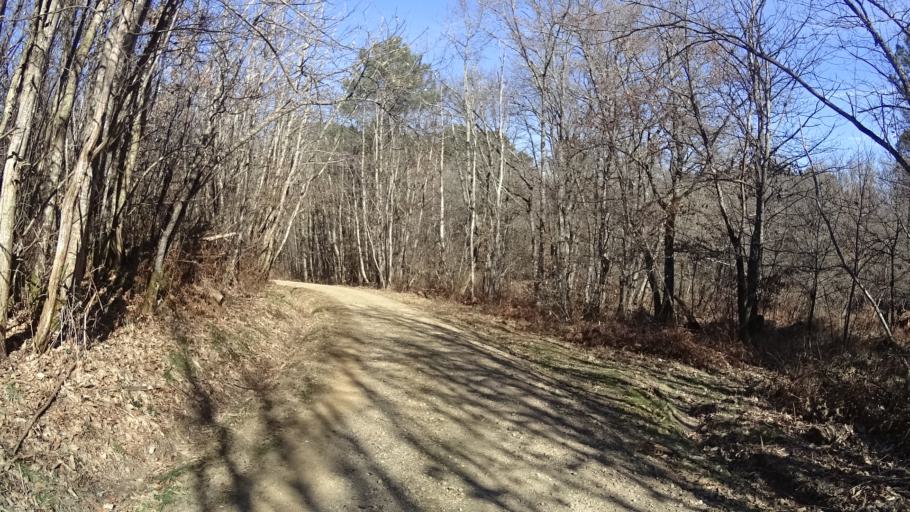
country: FR
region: Aquitaine
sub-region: Departement de la Dordogne
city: Riberac
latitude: 45.1948
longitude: 0.3170
